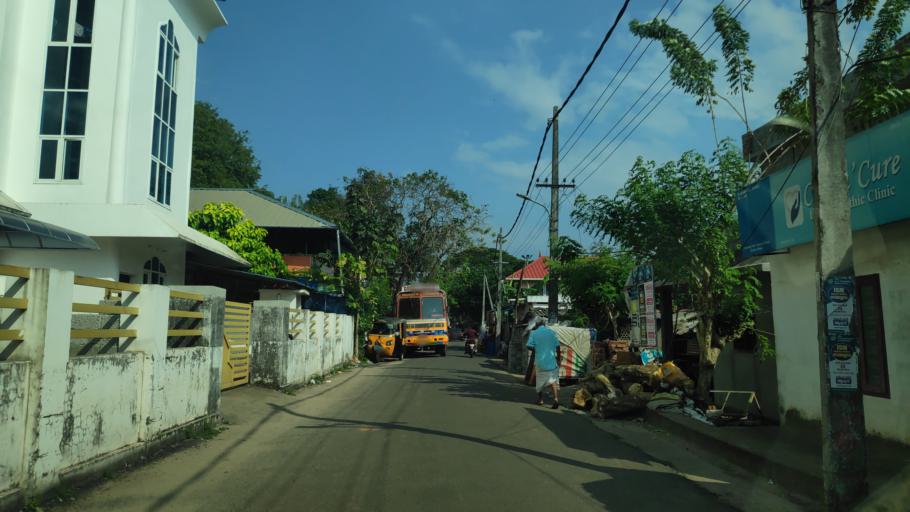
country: IN
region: Kerala
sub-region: Alappuzha
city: Alleppey
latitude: 9.5002
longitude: 76.3205
